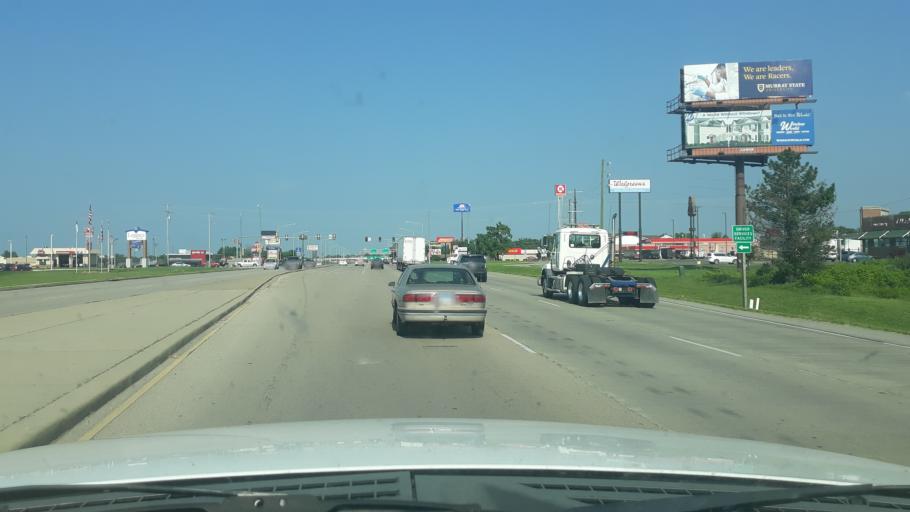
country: US
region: Illinois
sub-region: Williamson County
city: Marion
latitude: 37.7408
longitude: -88.9457
